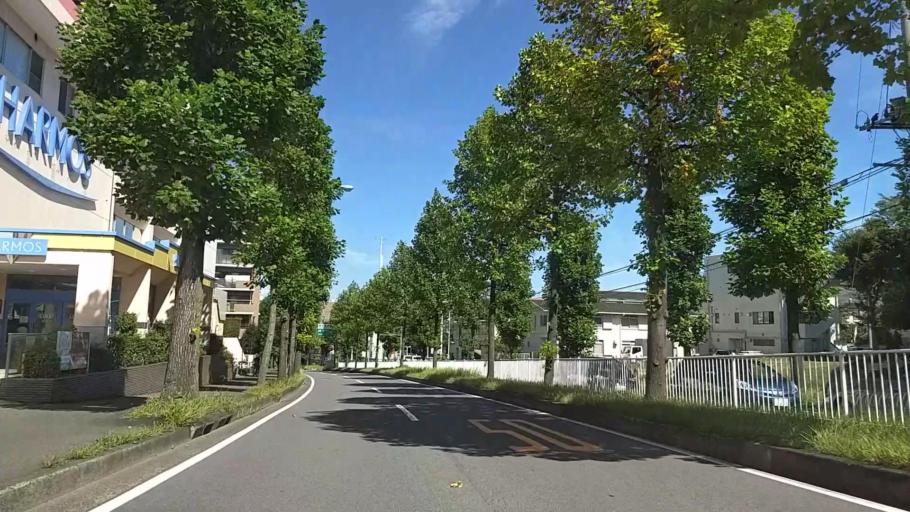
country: JP
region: Tokyo
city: Chofugaoka
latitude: 35.5552
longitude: 139.5547
